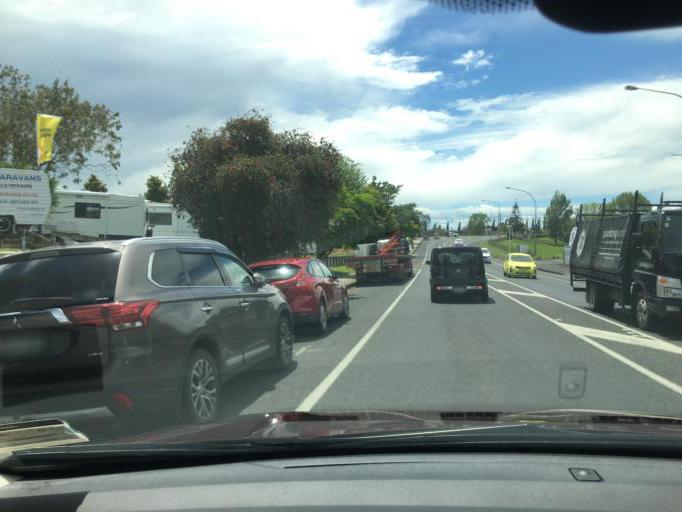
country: NZ
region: Waikato
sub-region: Hamilton City
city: Hamilton
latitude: -37.9183
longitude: 175.3067
